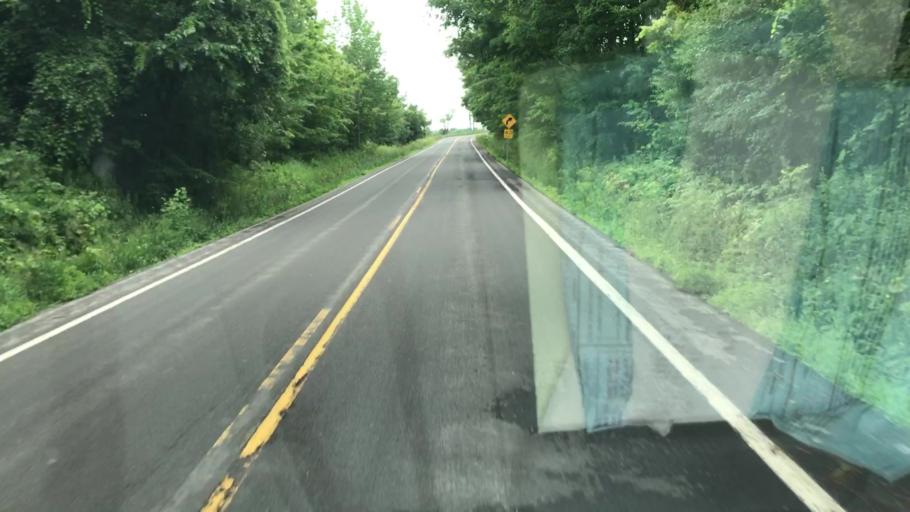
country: US
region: New York
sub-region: Onondaga County
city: Manlius
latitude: 42.9398
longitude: -75.9779
